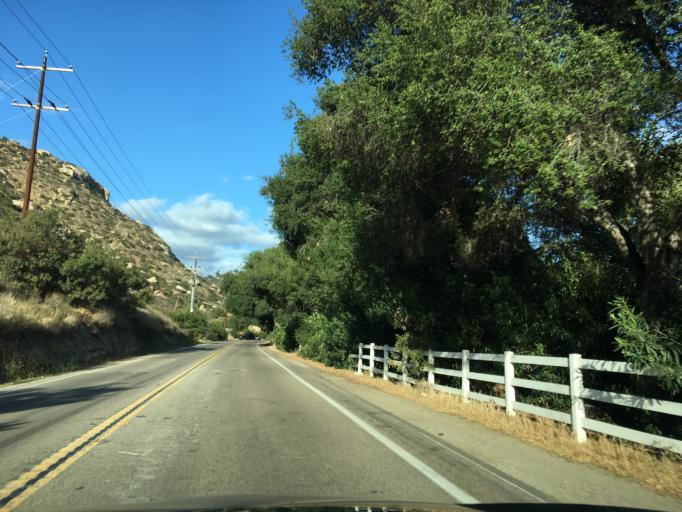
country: US
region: California
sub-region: San Diego County
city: Hidden Meadows
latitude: 33.2515
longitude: -117.1276
